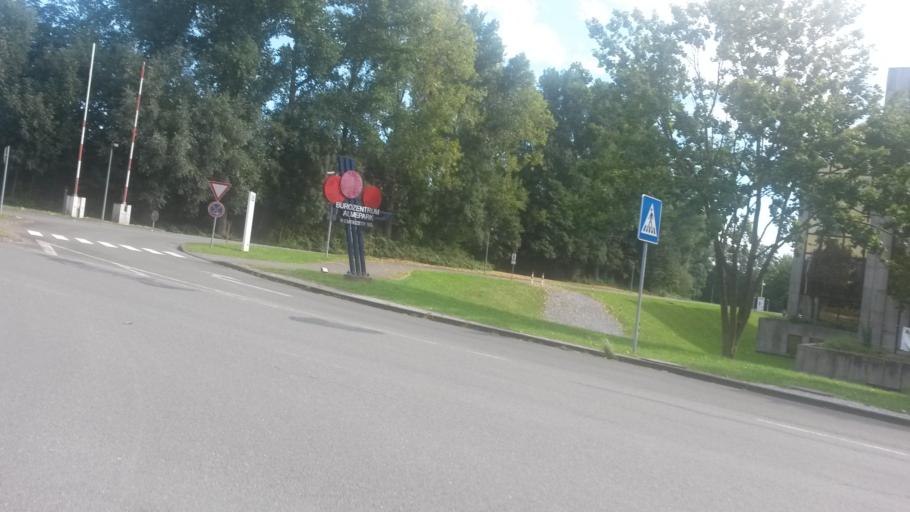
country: DE
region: North Rhine-Westphalia
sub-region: Regierungsbezirk Detmold
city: Paderborn
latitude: 51.7156
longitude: 8.7163
